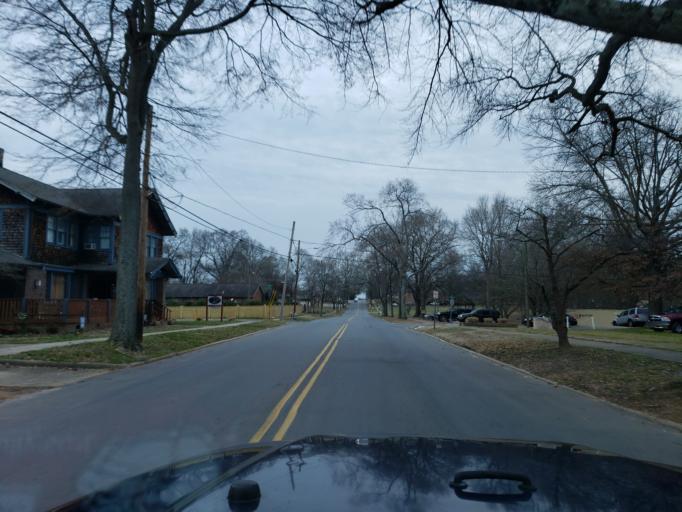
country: US
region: North Carolina
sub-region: Cleveland County
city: Shelby
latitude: 35.2967
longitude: -81.5417
